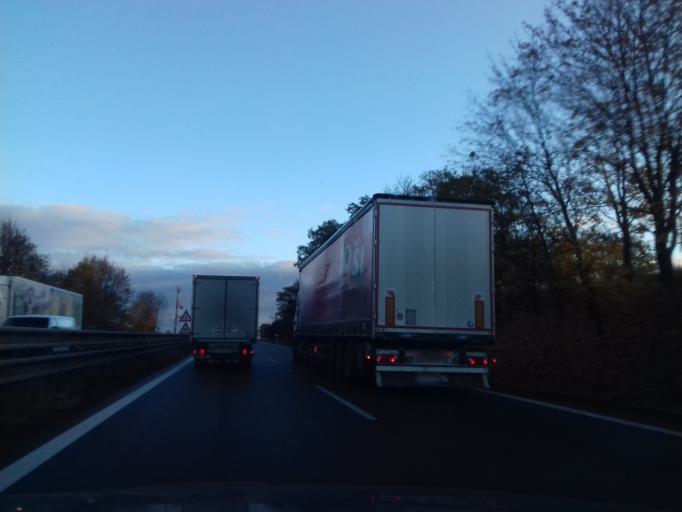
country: CZ
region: Olomoucky
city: Otaslavice
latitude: 49.3463
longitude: 17.0686
